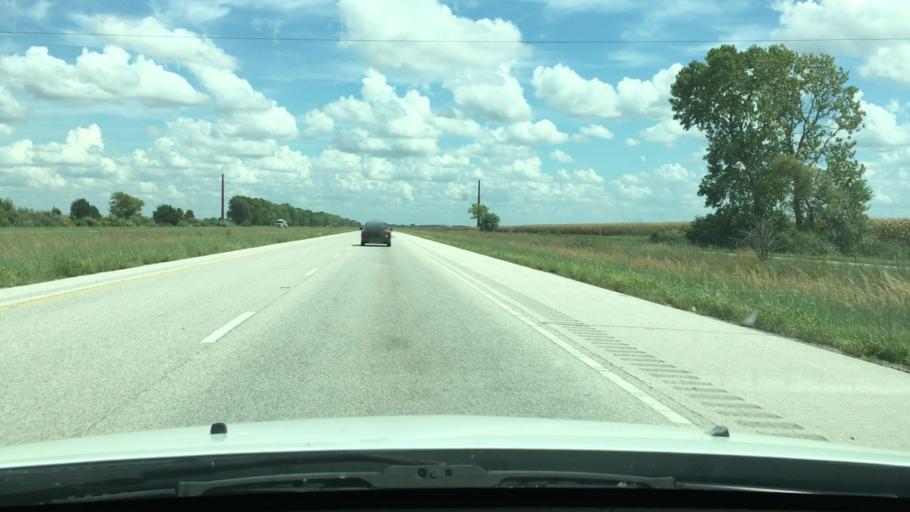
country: US
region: Illinois
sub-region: Scott County
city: Winchester
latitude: 39.6801
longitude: -90.3776
